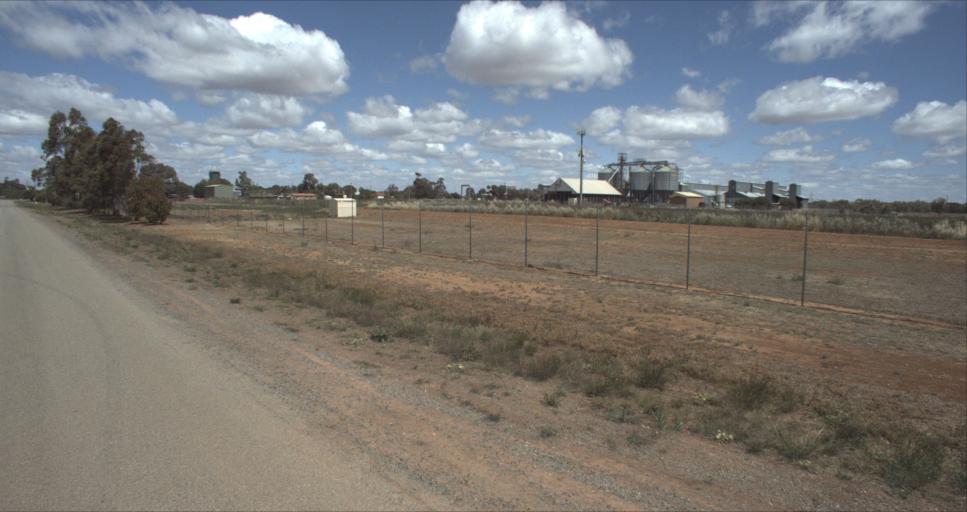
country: AU
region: New South Wales
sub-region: Murrumbidgee Shire
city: Darlington Point
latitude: -34.5124
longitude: 146.1845
